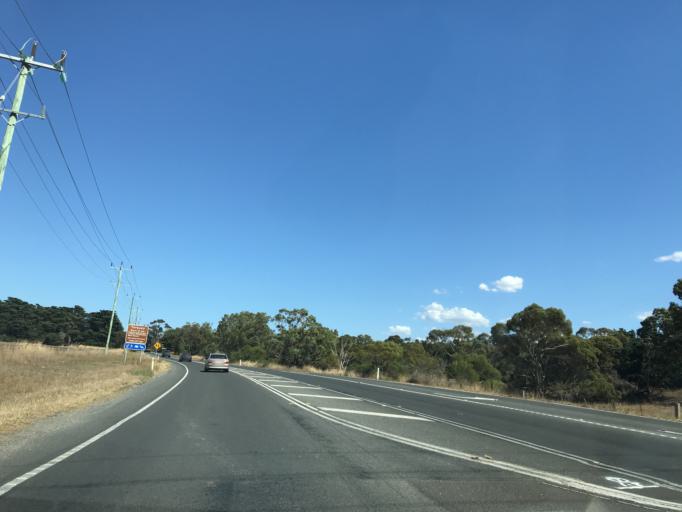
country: AU
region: Victoria
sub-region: Greater Geelong
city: Wandana Heights
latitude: -38.2274
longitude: 144.2806
